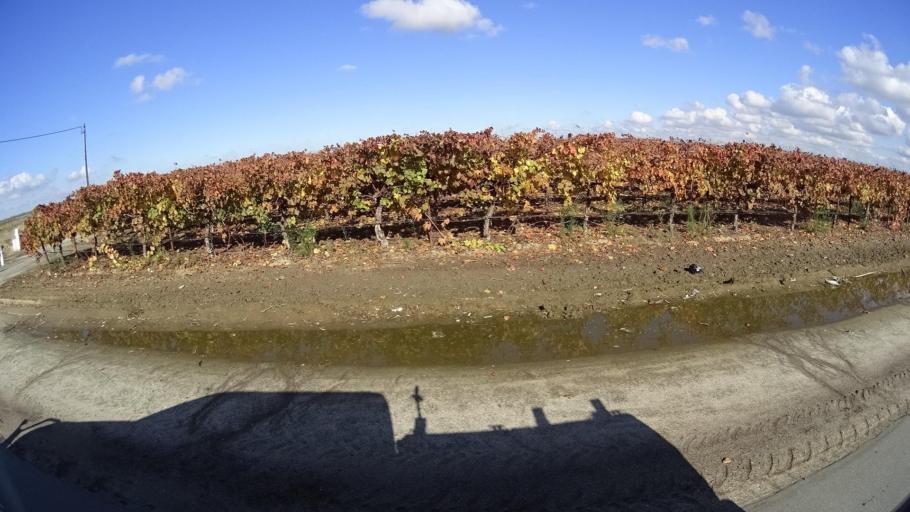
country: US
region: California
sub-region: Kern County
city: McFarland
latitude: 35.6743
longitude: -119.2540
